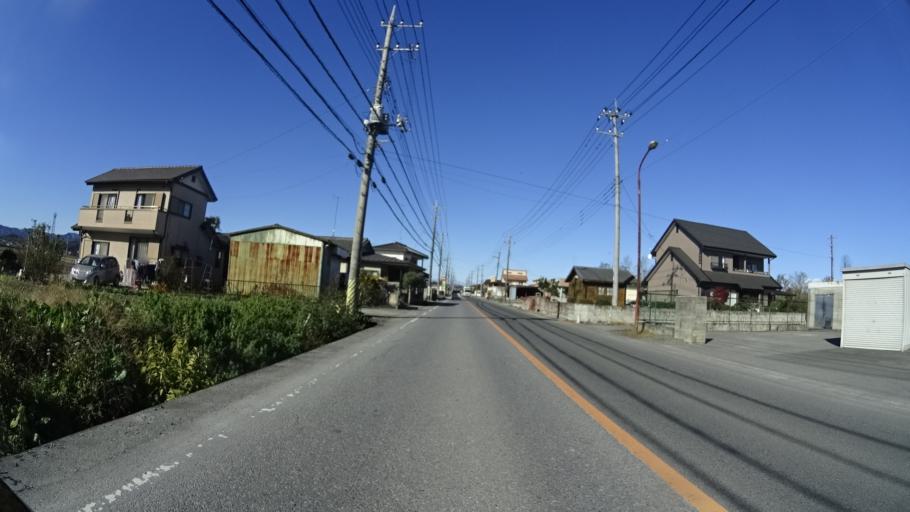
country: JP
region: Tochigi
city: Mibu
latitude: 36.4528
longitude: 139.7553
